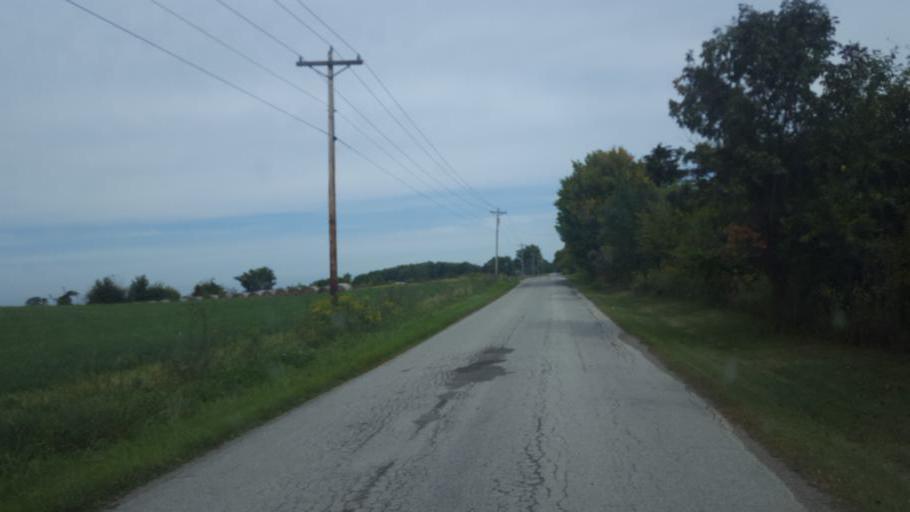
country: US
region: Ohio
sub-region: Knox County
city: Centerburg
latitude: 40.3575
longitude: -82.7252
